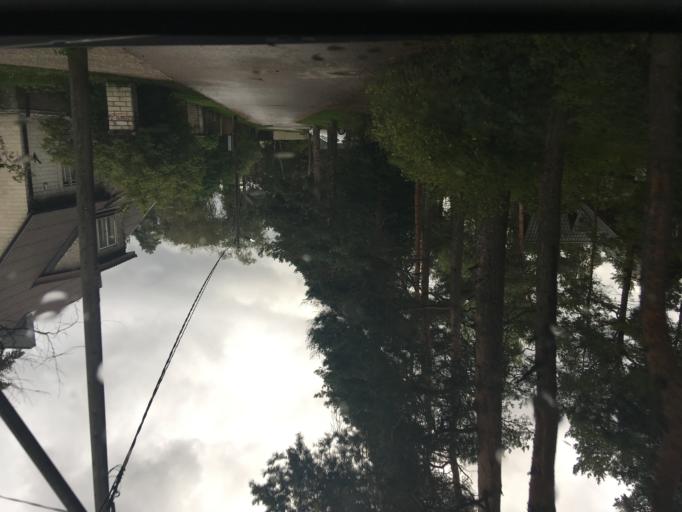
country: EE
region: Harju
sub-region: Saue vald
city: Laagri
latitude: 59.3639
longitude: 24.6467
